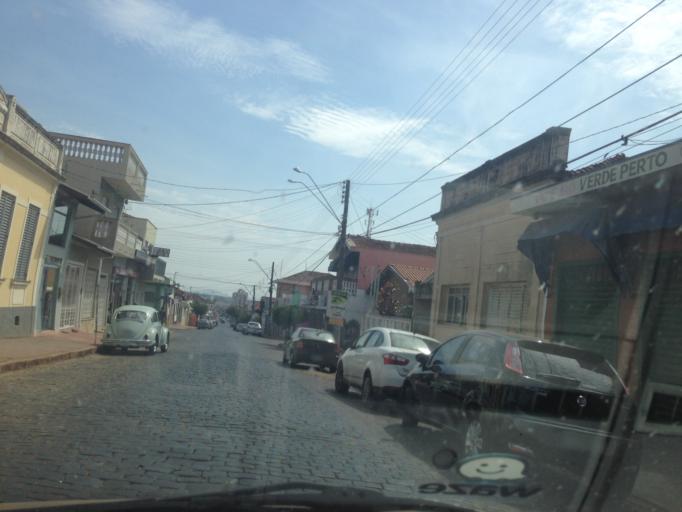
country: BR
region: Sao Paulo
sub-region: Casa Branca
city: Casa Branca
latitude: -21.7777
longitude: -47.0801
